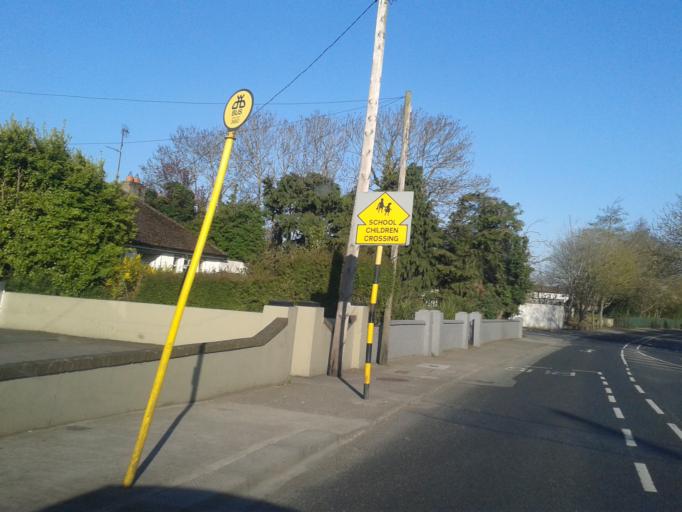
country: IE
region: Leinster
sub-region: Fingal County
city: Swords
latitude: 53.4620
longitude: -6.2309
